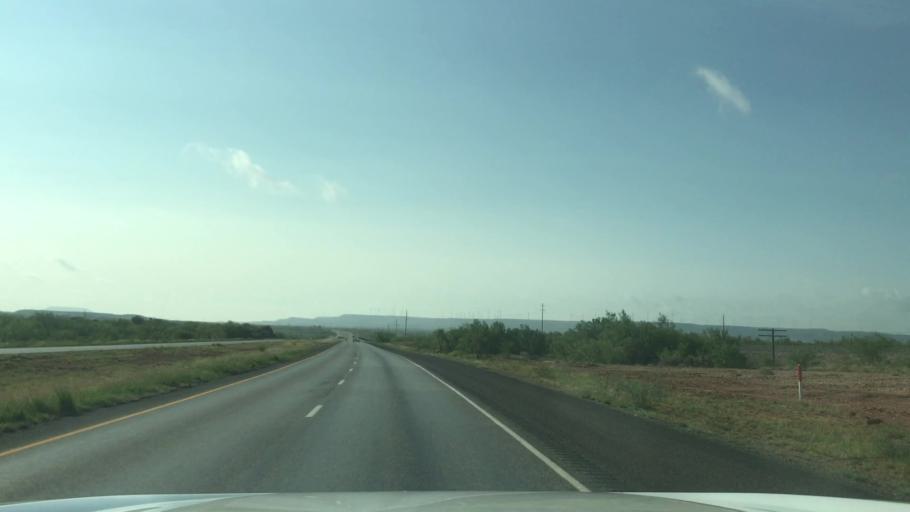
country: US
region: Texas
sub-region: Garza County
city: Post
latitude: 33.0133
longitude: -101.1755
